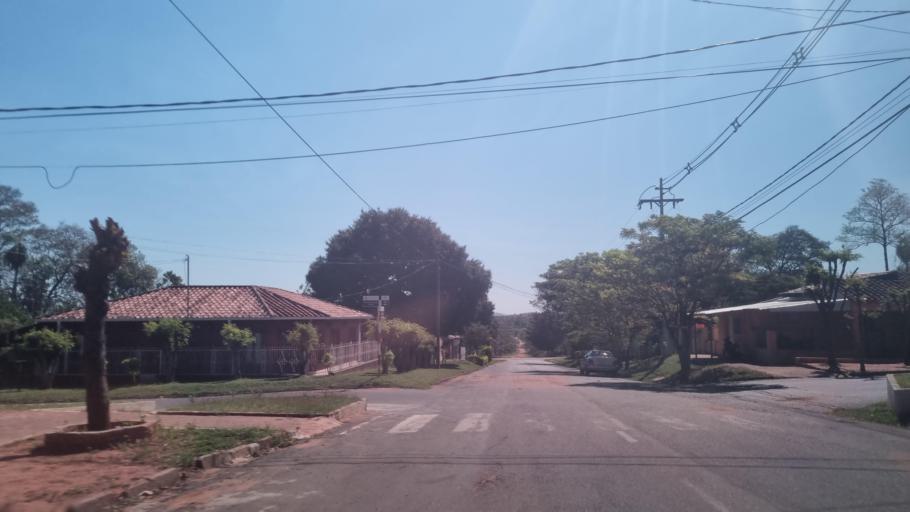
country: PY
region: Misiones
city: San Juan Bautista
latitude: -26.6655
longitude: -57.1434
